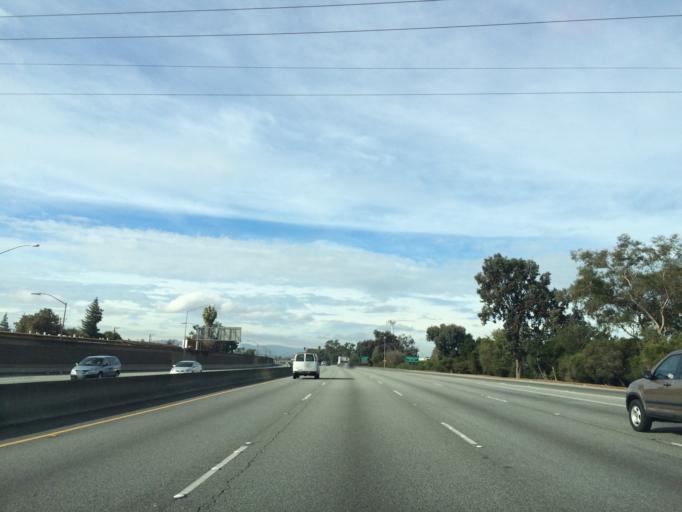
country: US
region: California
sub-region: San Mateo County
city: North Fair Oaks
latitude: 37.4840
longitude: -122.1823
